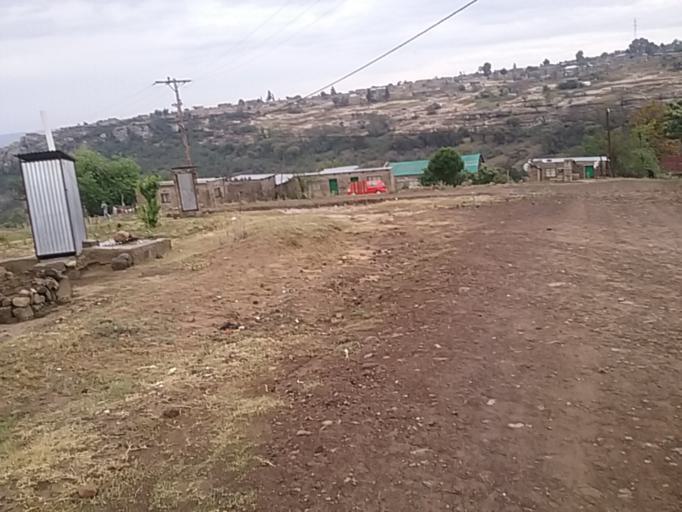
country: LS
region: Berea
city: Teyateyaneng
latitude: -29.1420
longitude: 27.7424
